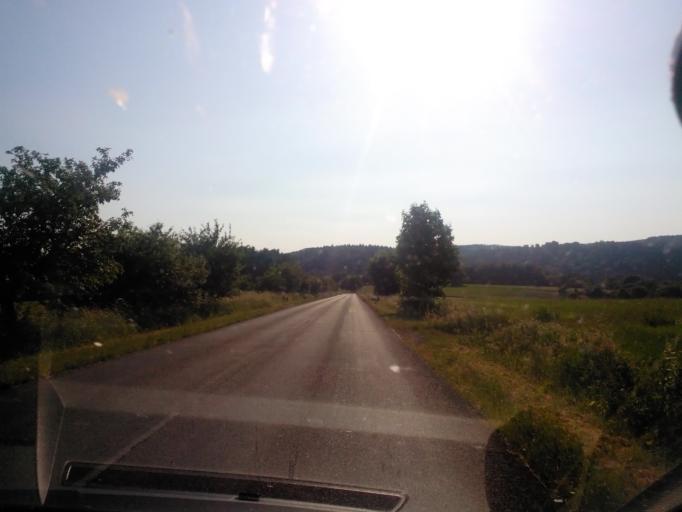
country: DE
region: Saarland
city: Beckingen
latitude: 49.4084
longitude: 6.7374
